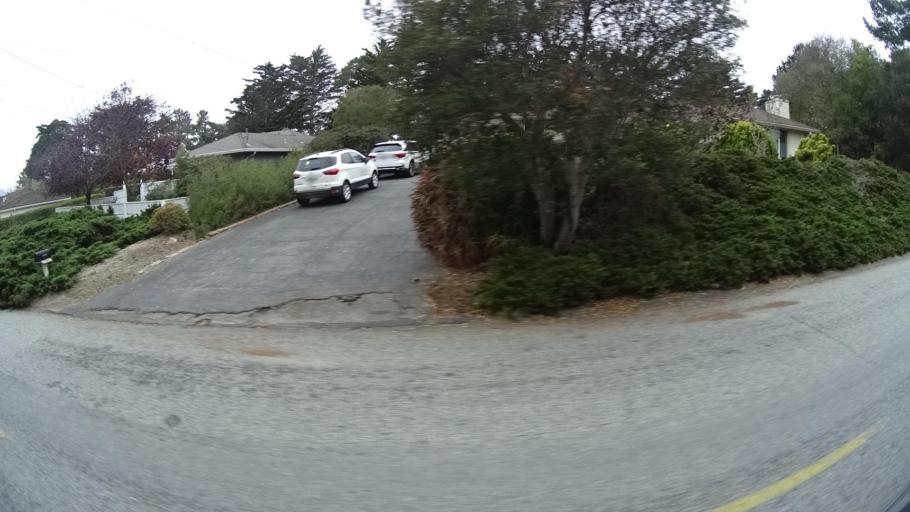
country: US
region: California
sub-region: Monterey County
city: Carmel-by-the-Sea
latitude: 36.5518
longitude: -121.9096
